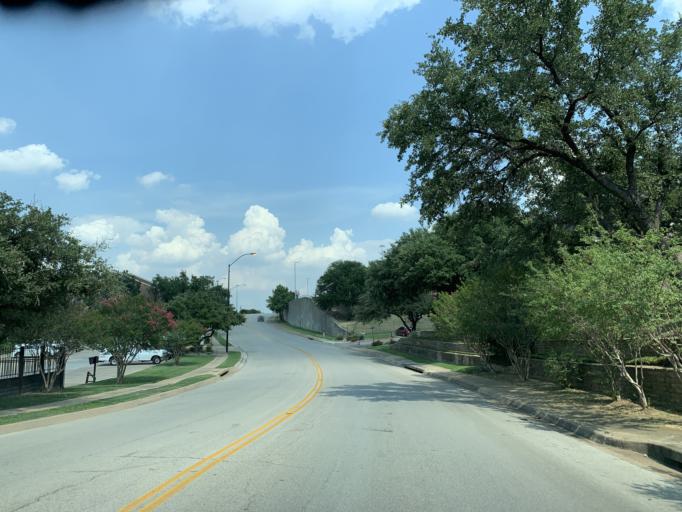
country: US
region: Texas
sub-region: Tarrant County
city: Richland Hills
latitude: 32.7682
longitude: -97.2170
